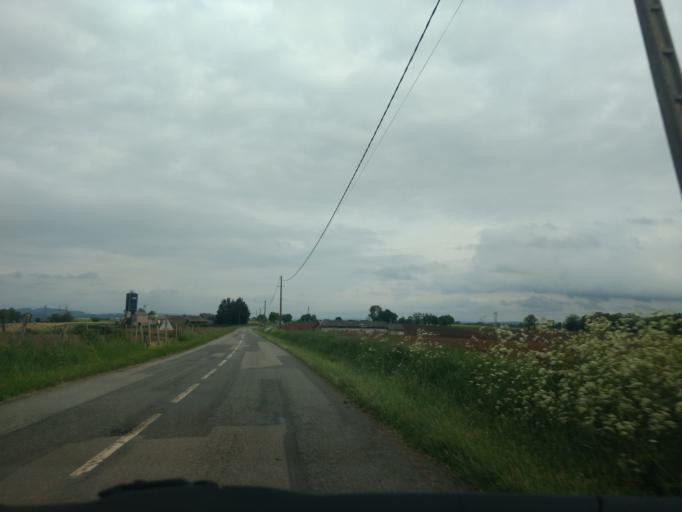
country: FR
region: Midi-Pyrenees
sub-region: Departement de l'Aveyron
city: Viviez
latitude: 44.5146
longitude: 2.1852
